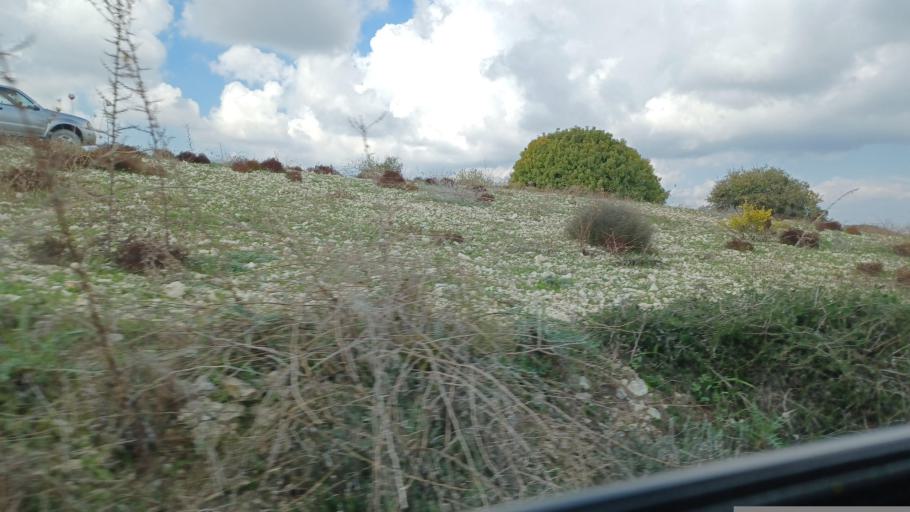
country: CY
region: Pafos
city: Mesogi
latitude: 34.8284
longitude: 32.5239
